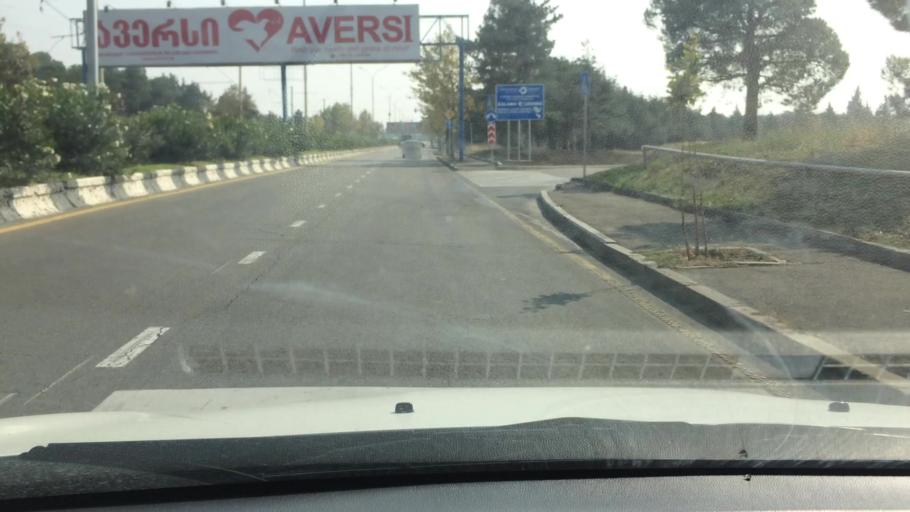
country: GE
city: Didi Lilo
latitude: 41.6773
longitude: 44.9598
